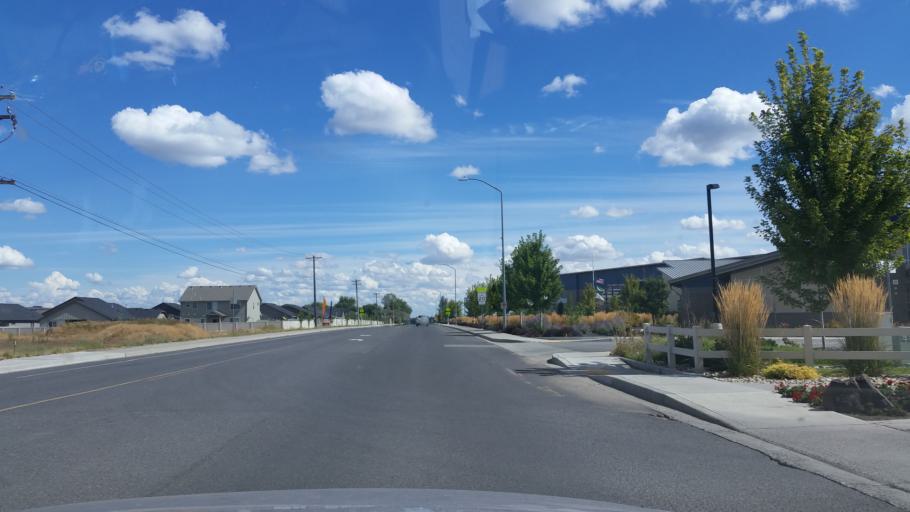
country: US
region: Washington
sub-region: Spokane County
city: Cheney
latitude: 47.5073
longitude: -117.5813
